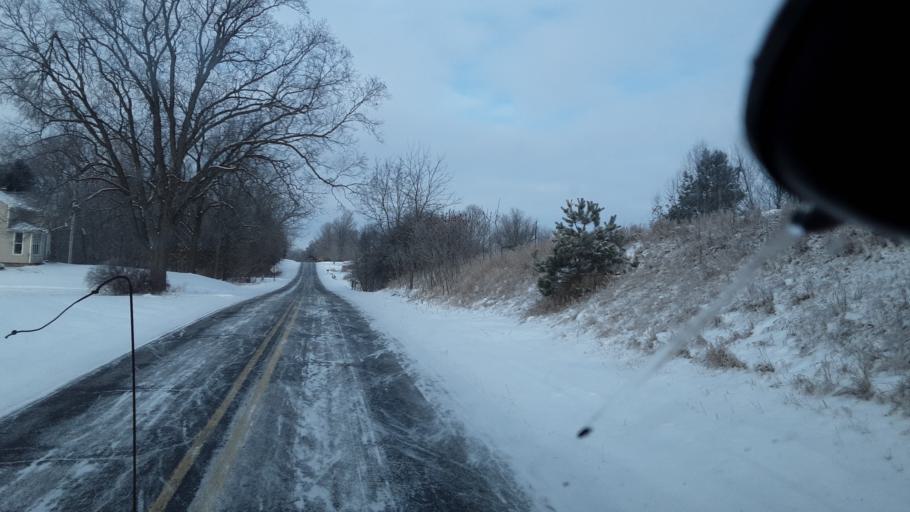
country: US
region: Michigan
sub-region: Ingham County
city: Leslie
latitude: 42.3689
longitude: -84.4843
